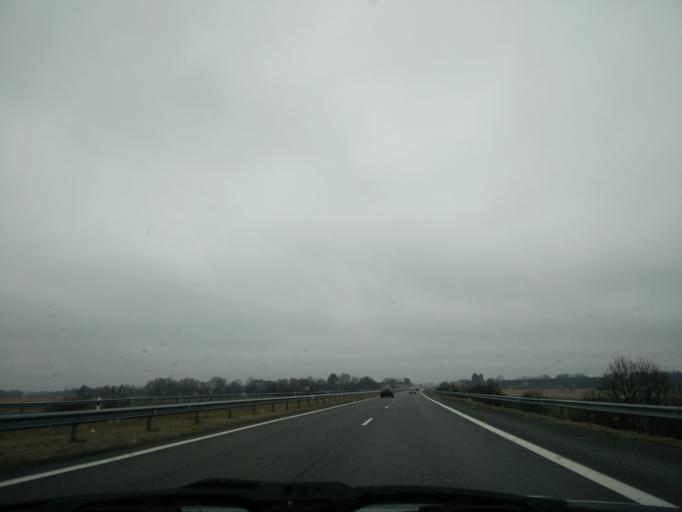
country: LT
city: Skaudvile
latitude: 55.4424
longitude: 22.7264
